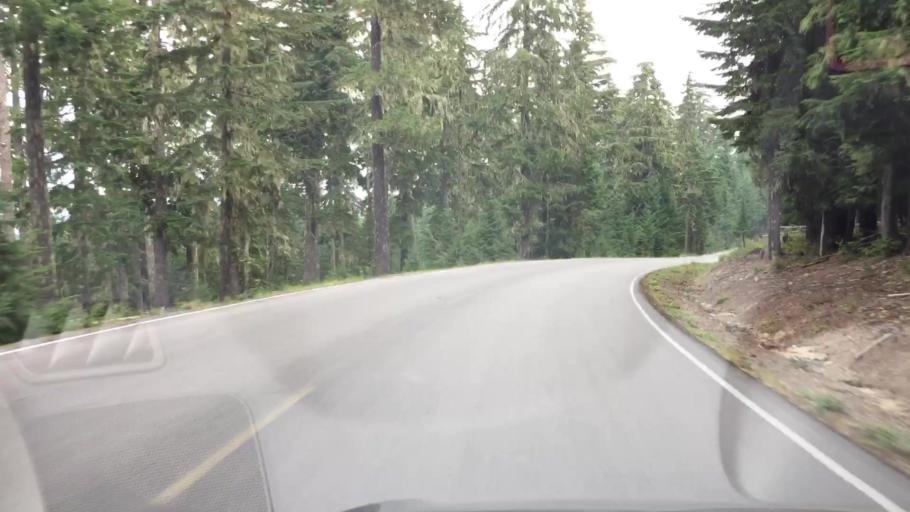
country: US
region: Washington
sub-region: Klickitat County
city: White Salmon
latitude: 46.2032
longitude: -121.6466
